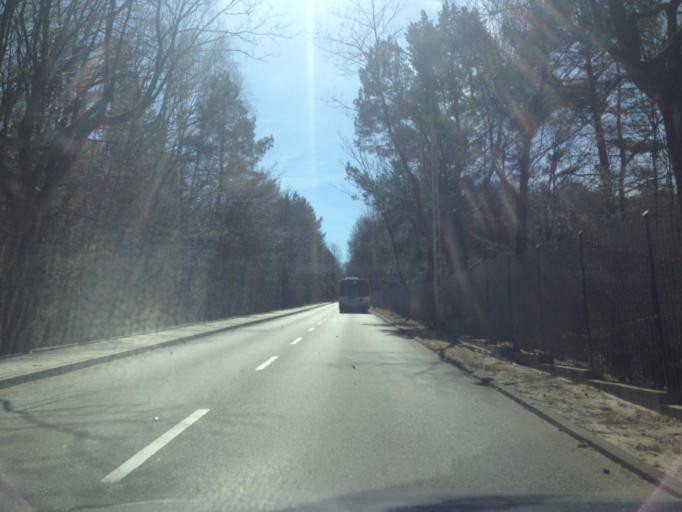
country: PL
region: Pomeranian Voivodeship
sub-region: Gdynia
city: Gdynia
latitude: 54.5070
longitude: 18.5155
